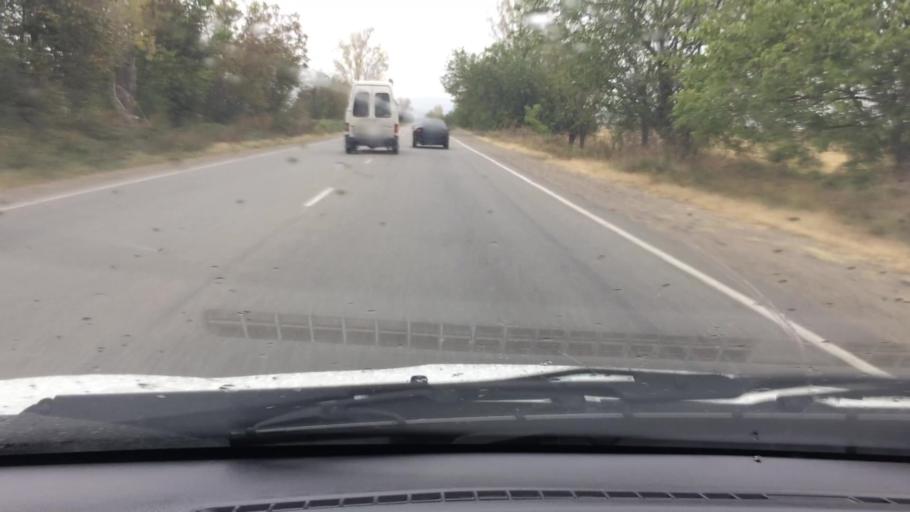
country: GE
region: Kvemo Kartli
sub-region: Marneuli
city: Marneuli
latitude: 41.5532
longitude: 44.7763
